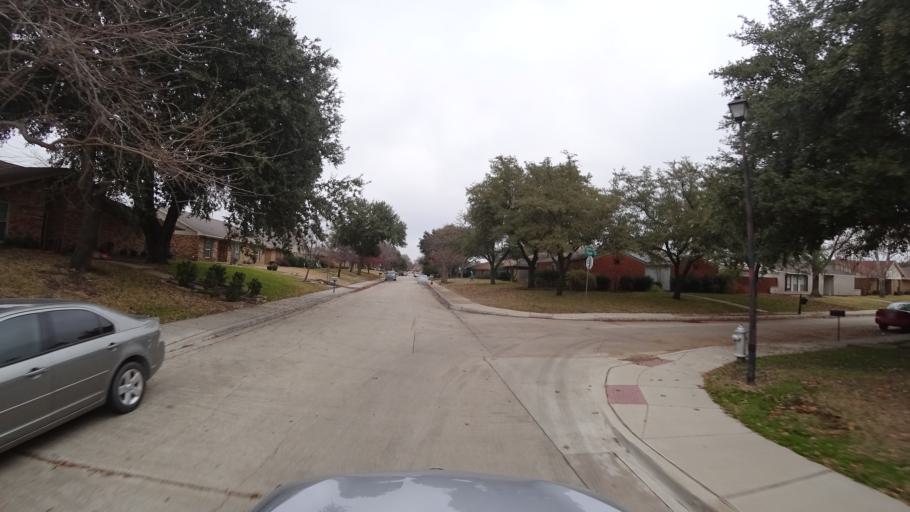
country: US
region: Texas
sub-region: Denton County
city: Highland Village
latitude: 33.0502
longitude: -97.0439
